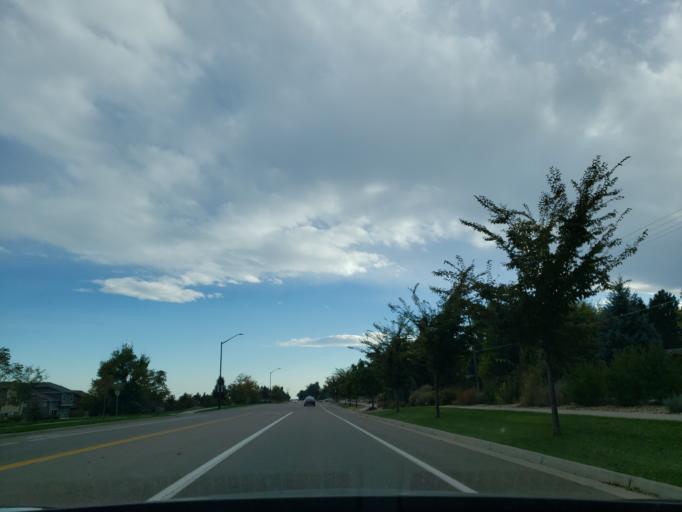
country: US
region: Colorado
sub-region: Larimer County
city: Fort Collins
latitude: 40.6199
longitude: -105.0388
